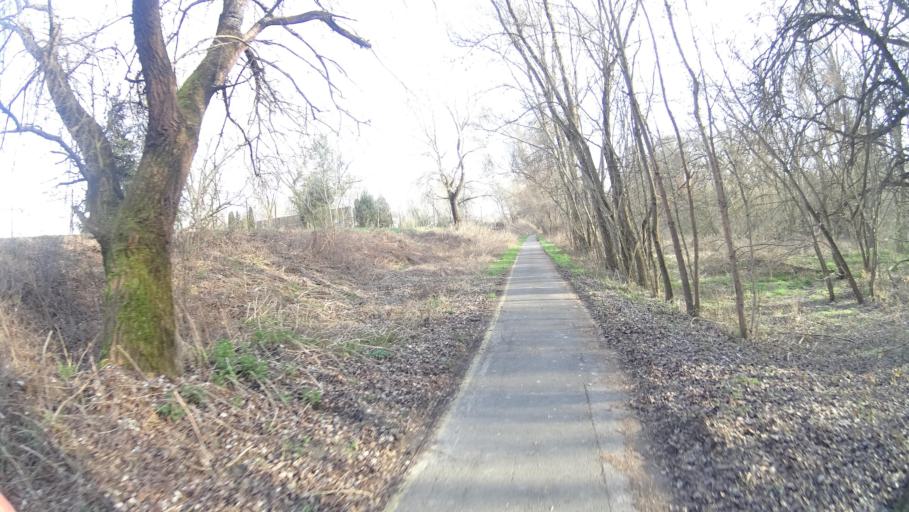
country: HU
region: Pest
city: Vac
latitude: 47.7616
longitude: 19.1364
